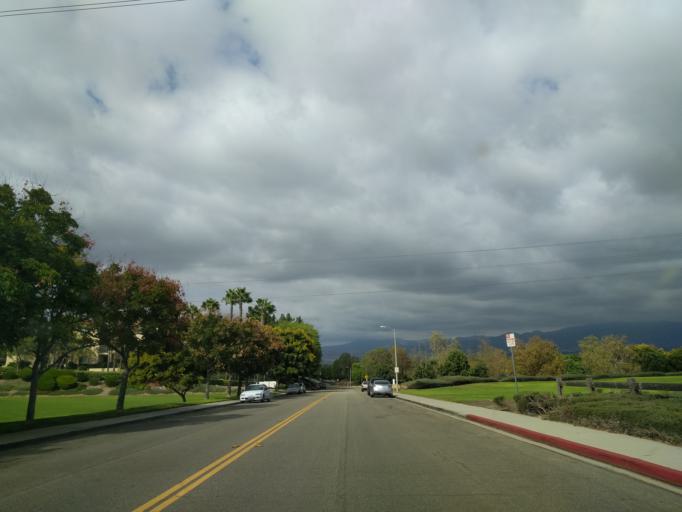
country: US
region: California
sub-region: Orange County
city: Laguna Woods
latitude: 33.5931
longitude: -117.7326
